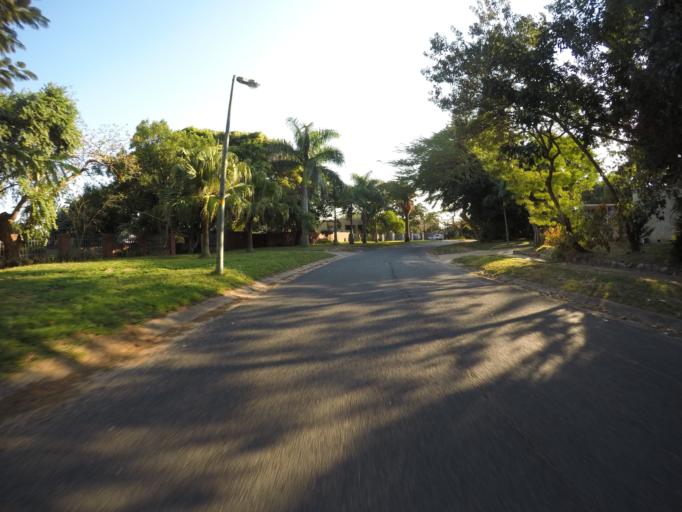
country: ZA
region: KwaZulu-Natal
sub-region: uThungulu District Municipality
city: Richards Bay
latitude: -28.7741
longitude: 32.1038
